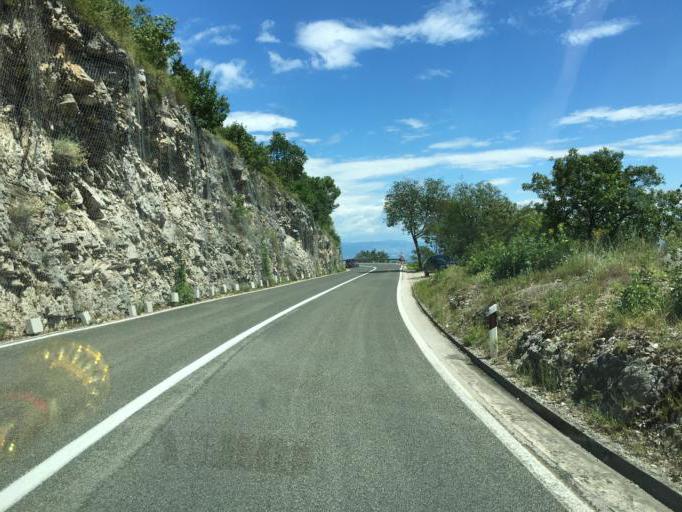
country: HR
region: Istarska
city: Lovran
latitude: 45.2123
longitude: 14.2422
